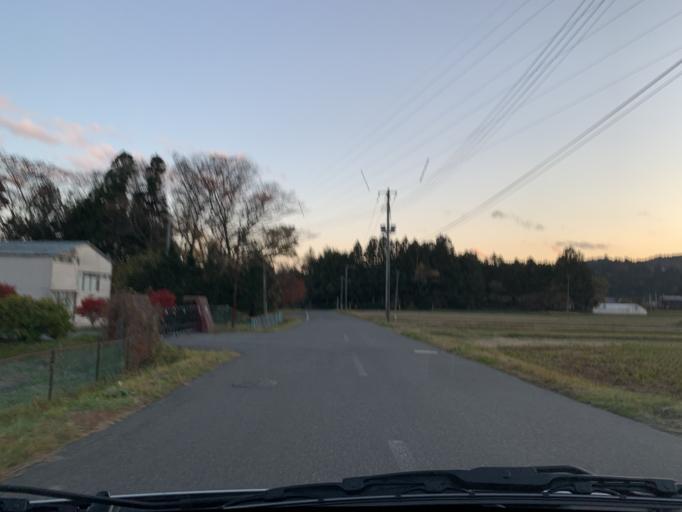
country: JP
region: Iwate
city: Ichinoseki
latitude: 39.0112
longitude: 141.1078
